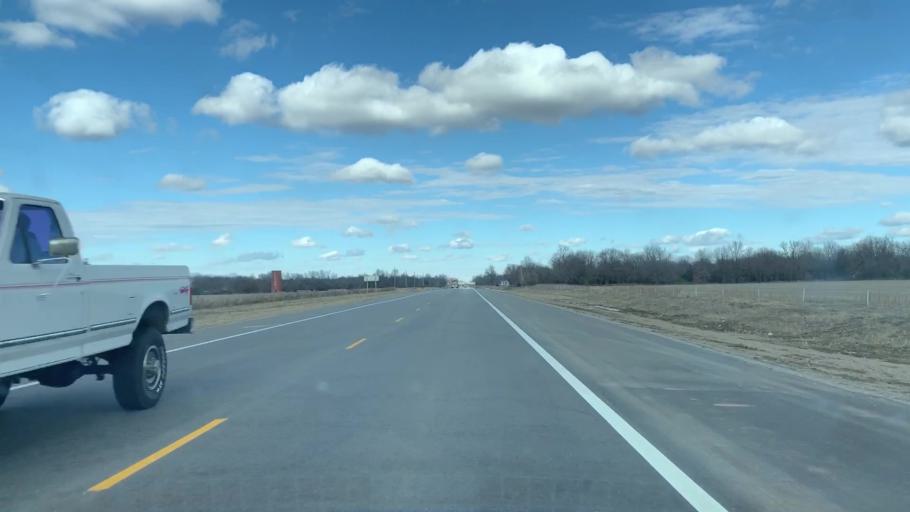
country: US
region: Kansas
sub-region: Cherokee County
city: Columbus
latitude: 37.2669
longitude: -94.8320
